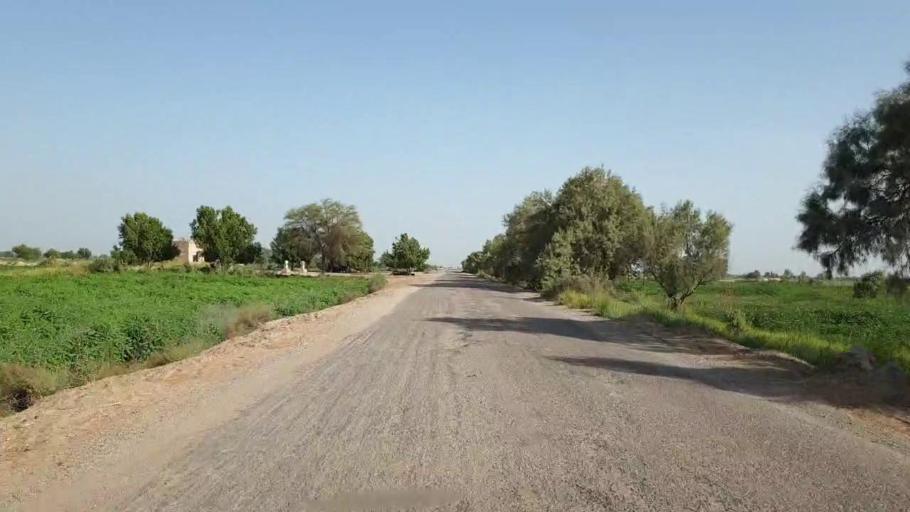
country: PK
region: Sindh
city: Nawabshah
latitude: 26.1558
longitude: 68.4458
